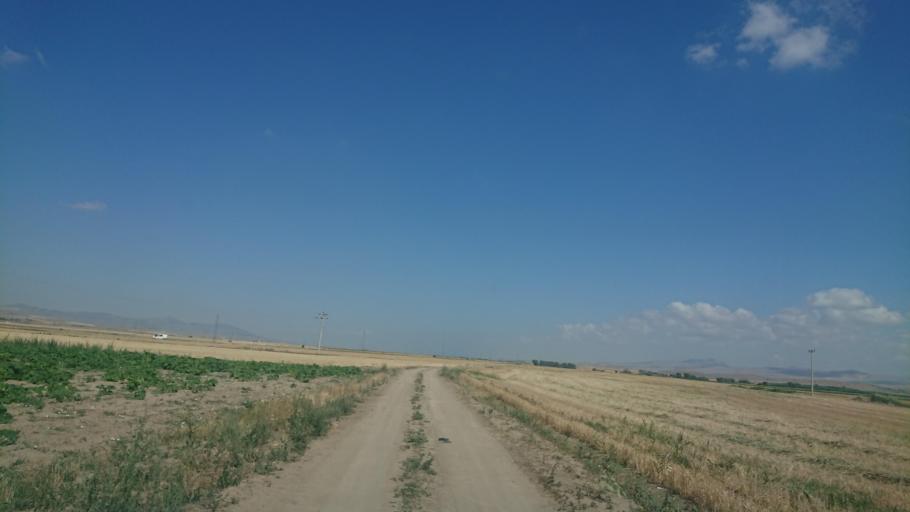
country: TR
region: Aksaray
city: Sariyahsi
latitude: 38.9854
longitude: 33.9047
